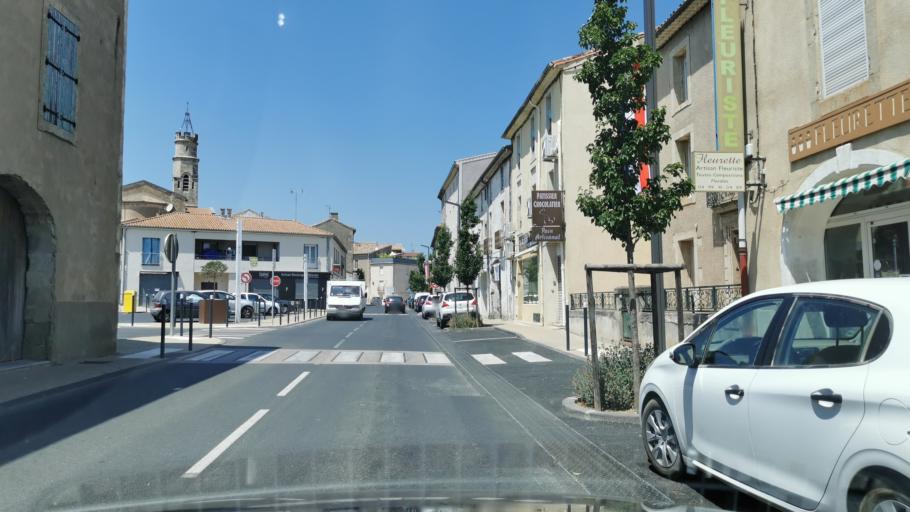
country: FR
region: Languedoc-Roussillon
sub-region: Departement de l'Herault
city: Cazouls-les-Beziers
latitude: 43.3916
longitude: 3.1034
